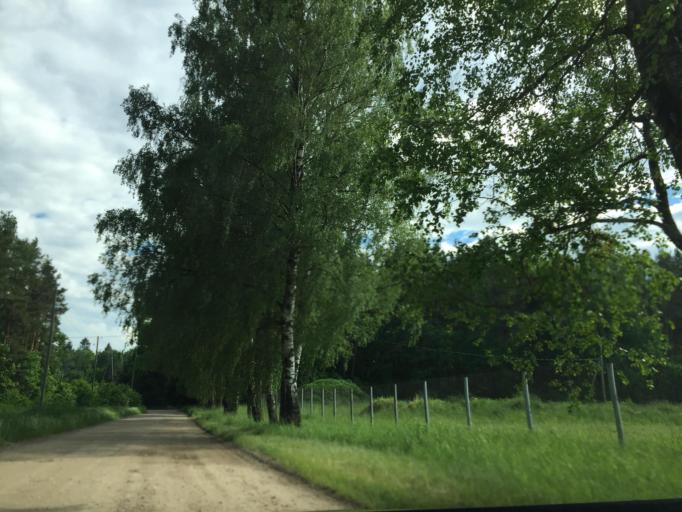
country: LV
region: Stopini
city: Ulbroka
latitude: 56.9299
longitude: 24.2890
